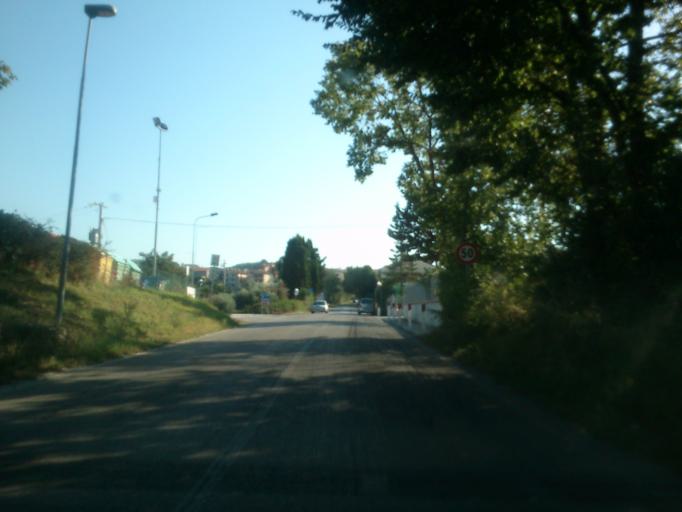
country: IT
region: The Marches
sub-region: Provincia di Pesaro e Urbino
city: Mombaroccio
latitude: 43.8116
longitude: 12.8605
